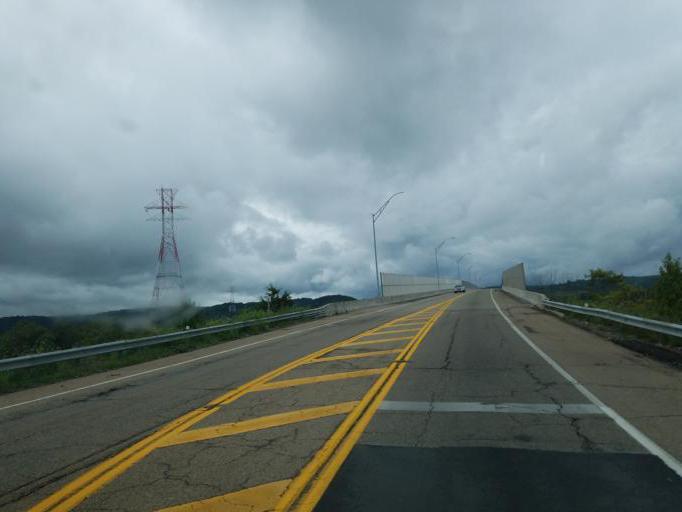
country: US
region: Ohio
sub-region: Scioto County
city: Franklin Furnace
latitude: 38.6473
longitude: -82.8535
